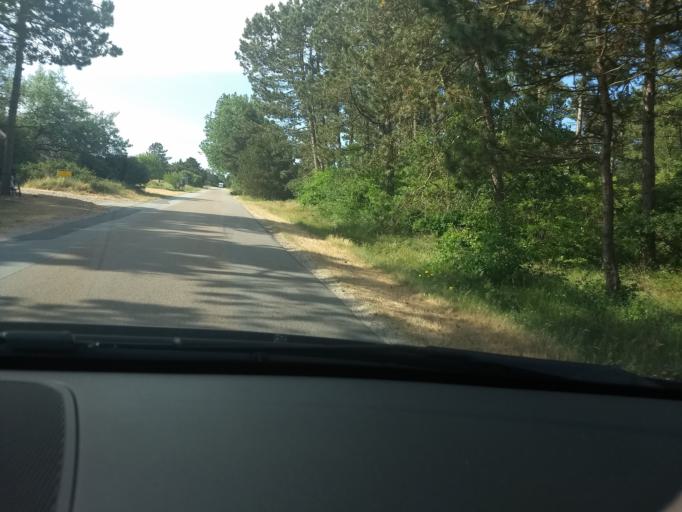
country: DE
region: Schleswig-Holstein
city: List
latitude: 55.0931
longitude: 8.5431
